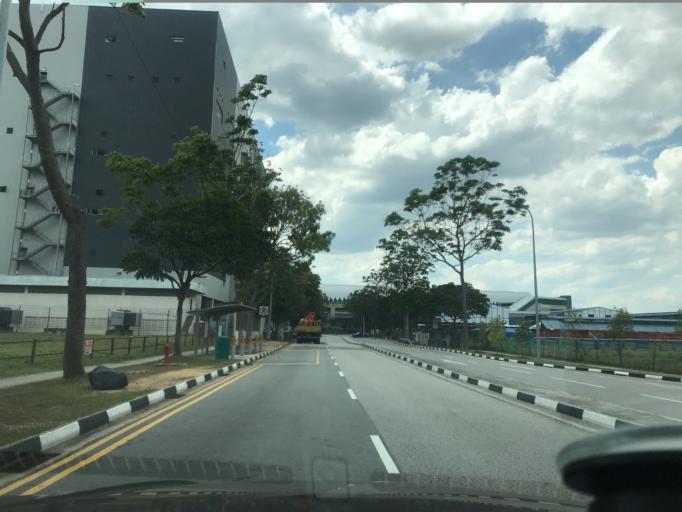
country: MY
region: Johor
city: Johor Bahru
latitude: 1.3384
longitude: 103.6385
